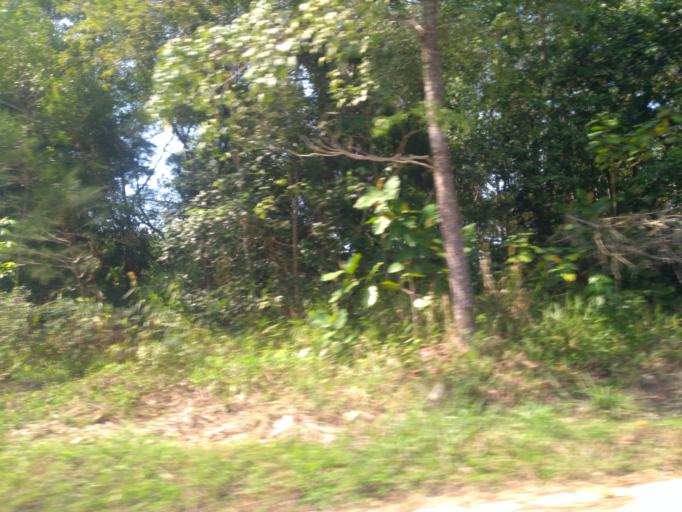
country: MY
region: Sarawak
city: Kuching
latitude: 1.7460
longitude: 110.3152
